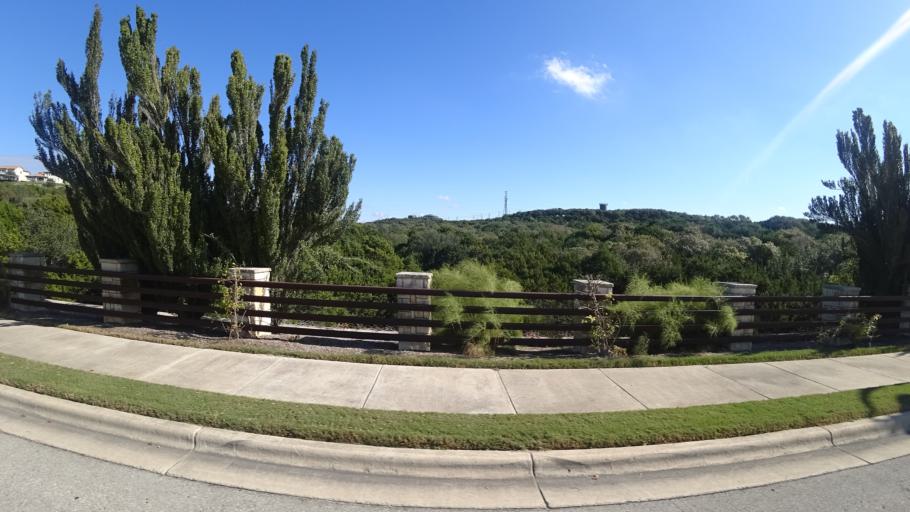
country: US
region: Texas
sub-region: Travis County
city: Hudson Bend
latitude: 30.3681
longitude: -97.8911
